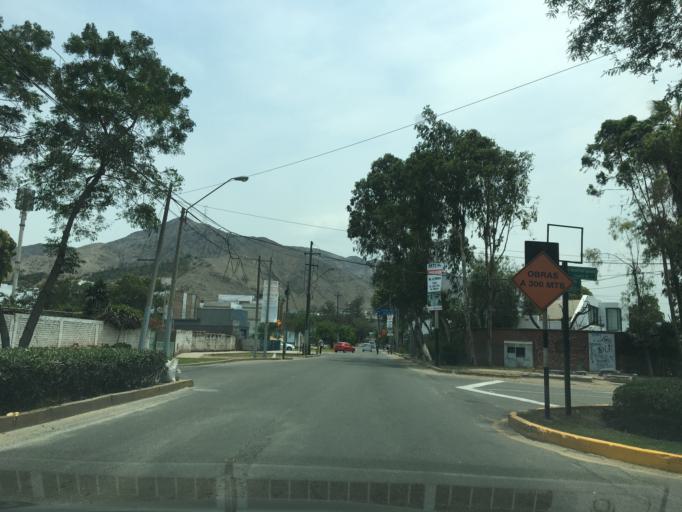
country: PE
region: Lima
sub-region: Lima
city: La Molina
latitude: -12.0762
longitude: -76.9403
